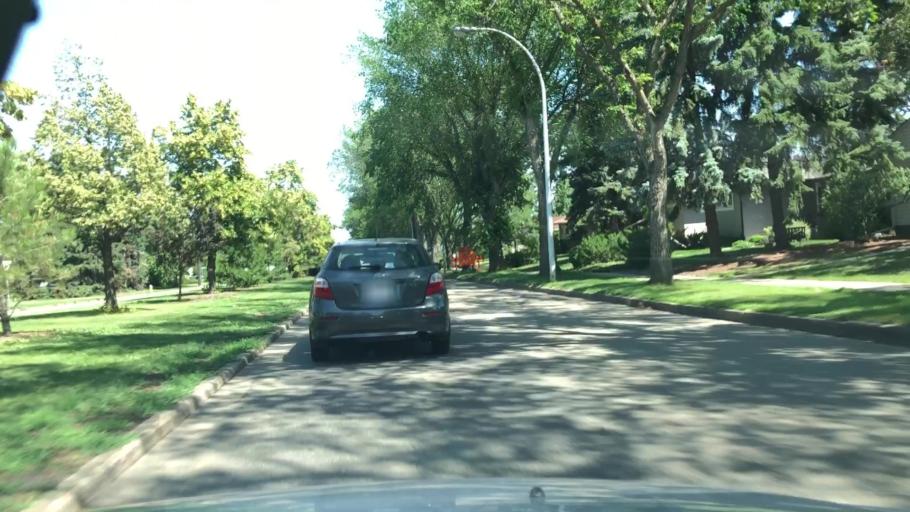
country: CA
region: Alberta
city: Edmonton
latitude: 53.5488
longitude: -113.4185
